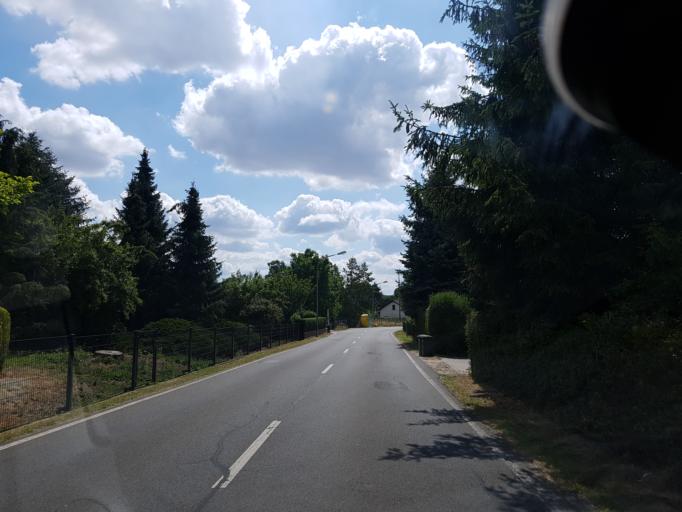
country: DE
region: Brandenburg
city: Drebkau
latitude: 51.6859
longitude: 14.2733
